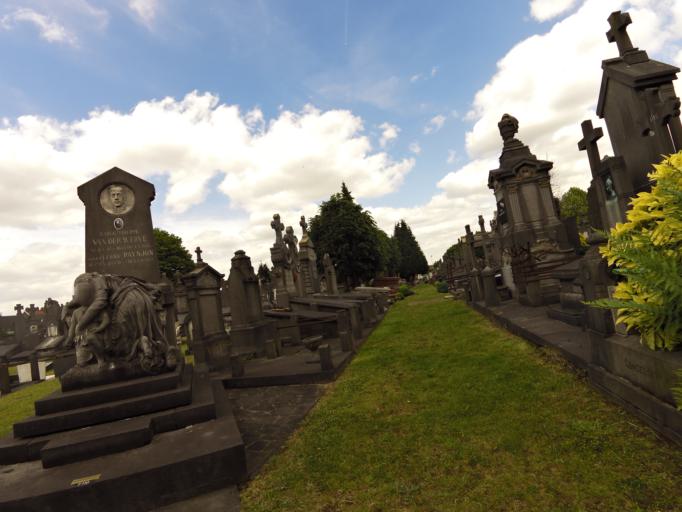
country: BE
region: Flanders
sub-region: Provincie Oost-Vlaanderen
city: Ledeberg
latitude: 51.0637
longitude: 3.7496
